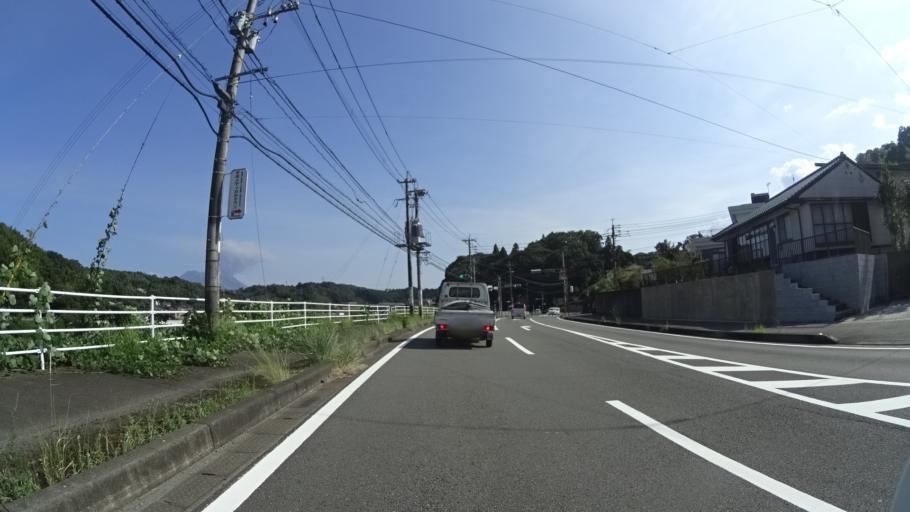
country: JP
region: Kagoshima
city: Kagoshima-shi
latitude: 31.6558
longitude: 130.5502
